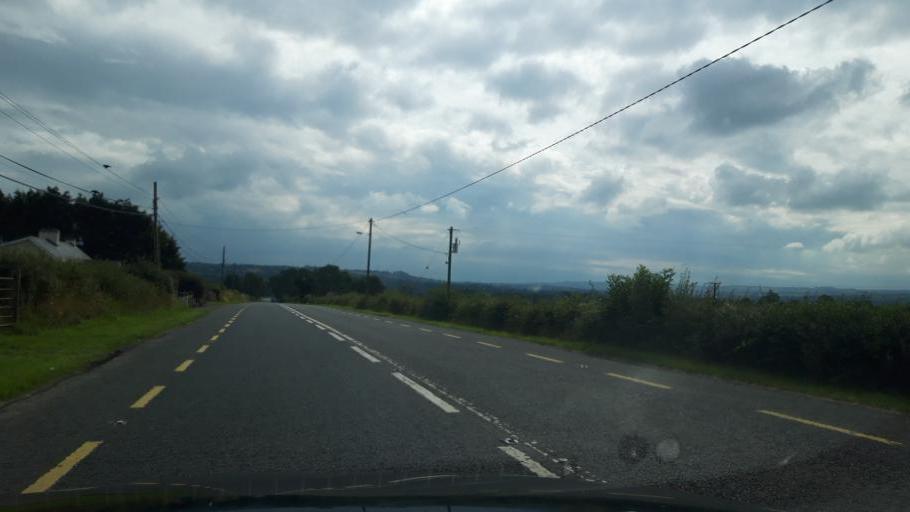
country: IE
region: Leinster
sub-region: Kilkenny
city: Castlecomer
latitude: 52.8555
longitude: -7.1177
